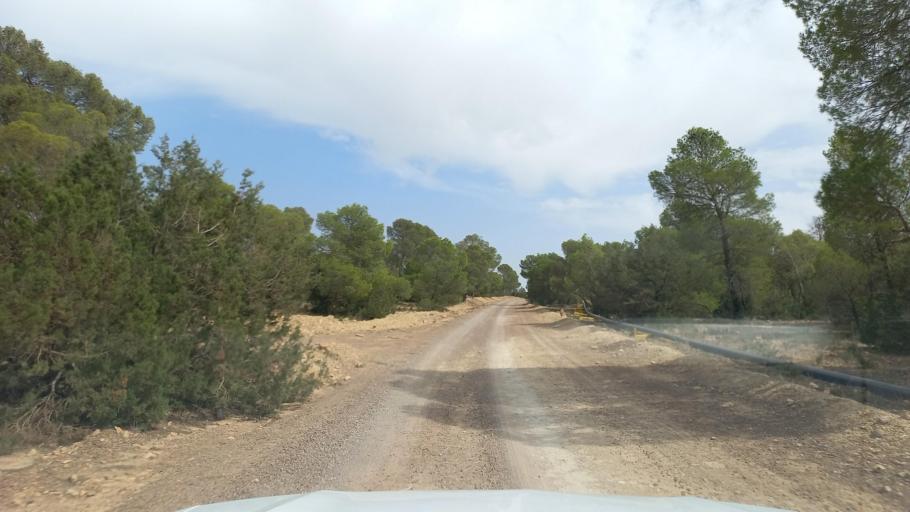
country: TN
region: Al Qasrayn
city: Kasserine
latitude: 35.3821
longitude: 8.8897
